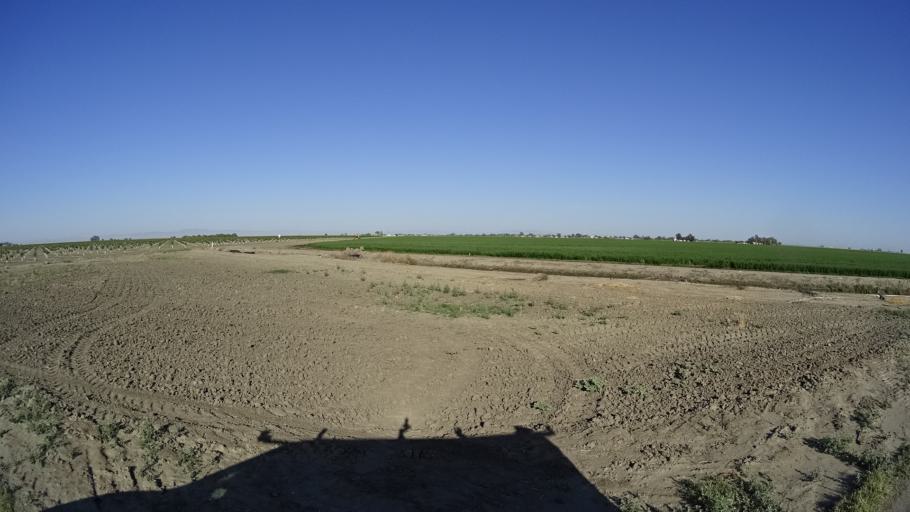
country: US
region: California
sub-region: Kings County
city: Stratford
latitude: 36.1827
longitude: -119.7983
